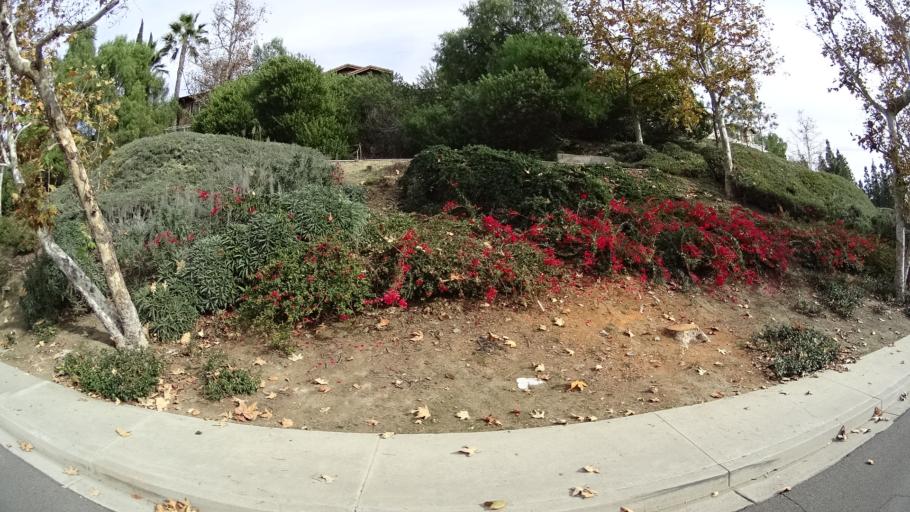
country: US
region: California
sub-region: Orange County
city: Aliso Viejo
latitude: 33.5826
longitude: -117.7400
